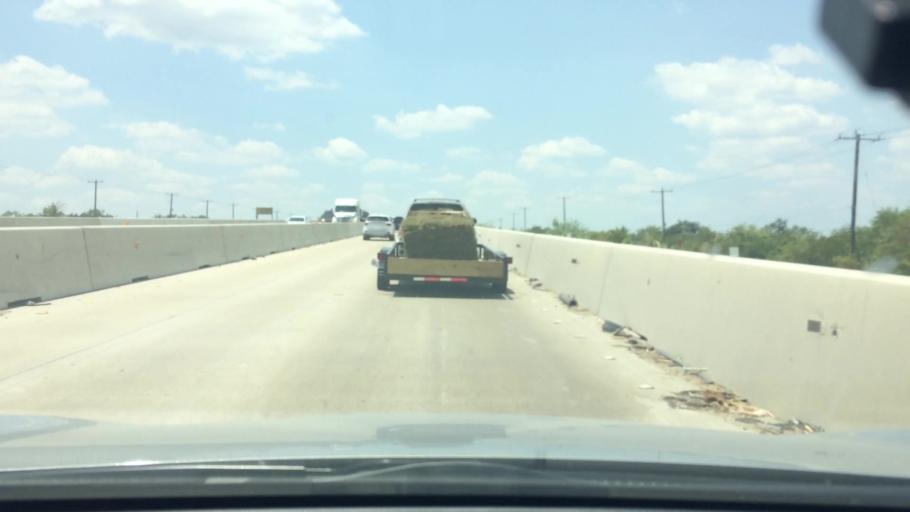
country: US
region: Texas
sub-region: Bexar County
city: Kirby
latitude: 29.4518
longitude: -98.3422
